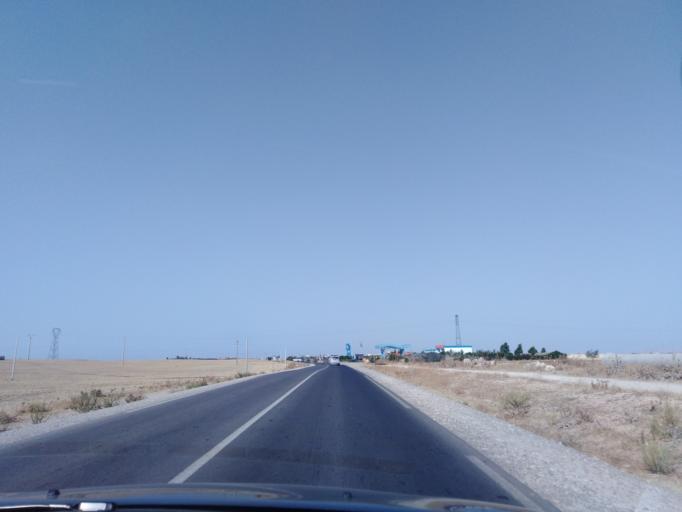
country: MA
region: Doukkala-Abda
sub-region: Safi
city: Safi
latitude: 32.2646
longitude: -8.9524
